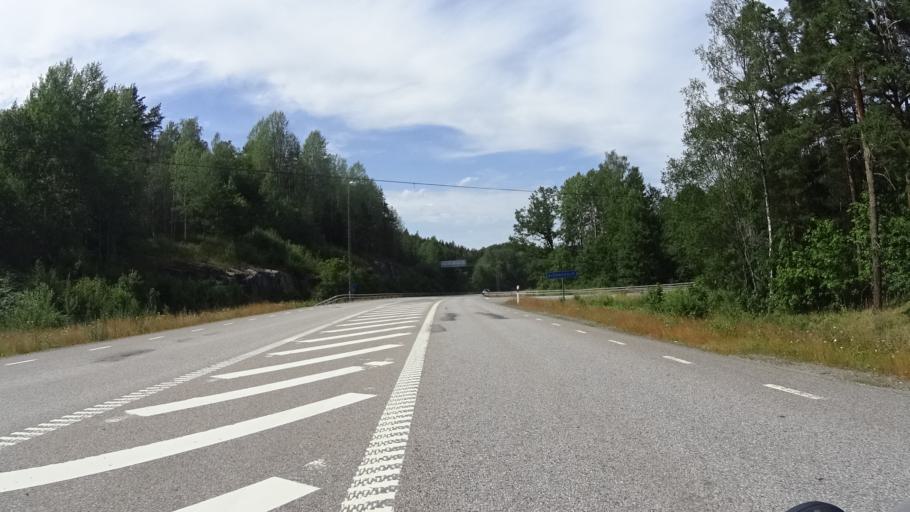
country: SE
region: Kalmar
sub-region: Vasterviks Kommun
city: Overum
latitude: 57.9753
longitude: 16.3326
